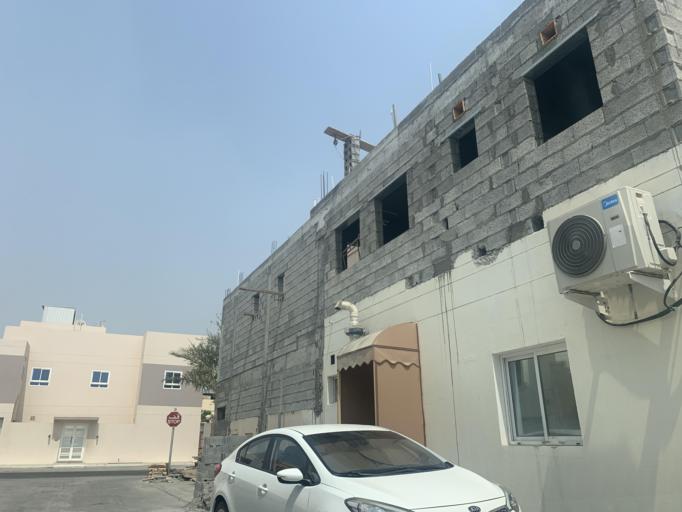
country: BH
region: Manama
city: Jidd Hafs
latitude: 26.2114
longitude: 50.5068
